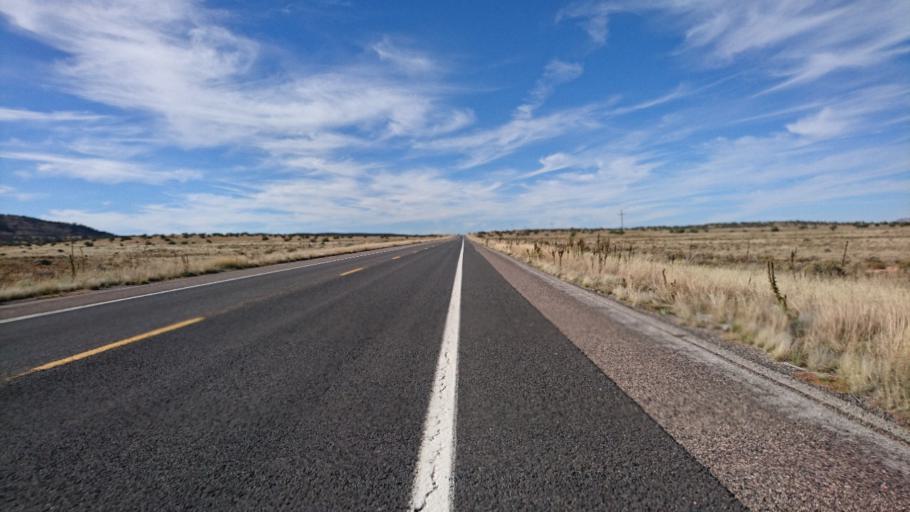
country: US
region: Arizona
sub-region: Mohave County
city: Peach Springs
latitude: 35.4903
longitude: -113.1565
